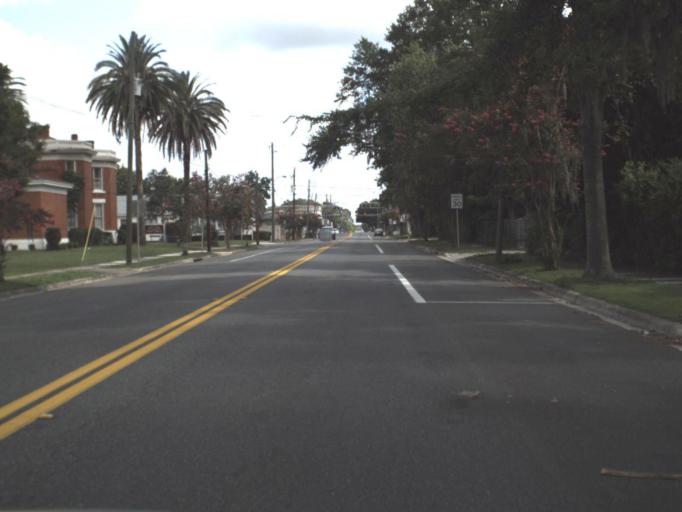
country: US
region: Florida
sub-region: Baker County
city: Macclenny
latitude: 30.2796
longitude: -82.1217
